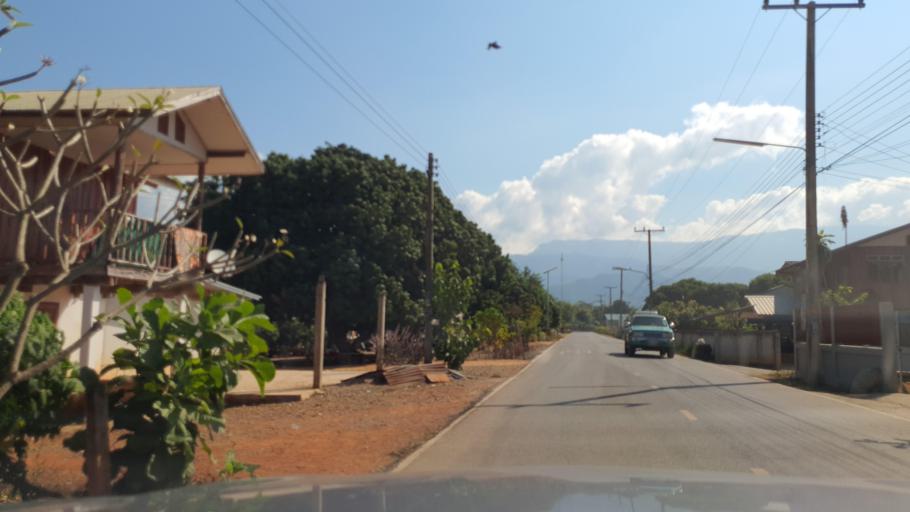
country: TH
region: Nan
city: Pua
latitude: 19.1446
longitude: 100.9224
